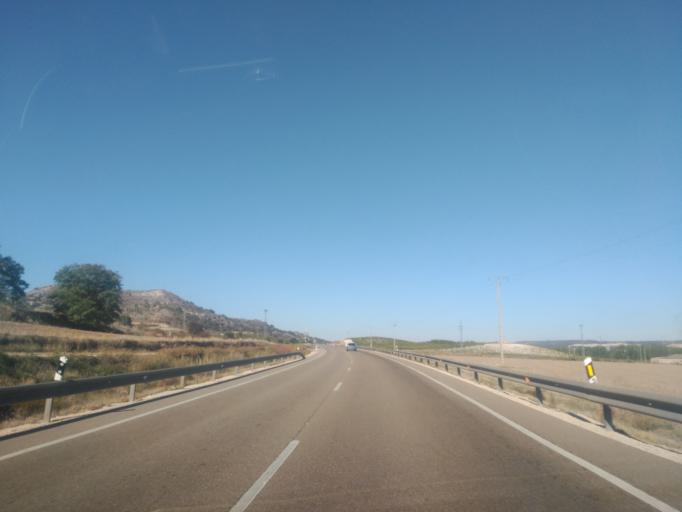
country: ES
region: Castille and Leon
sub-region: Provincia de Valladolid
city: Quintanilla de Arriba
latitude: 41.6233
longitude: -4.2553
